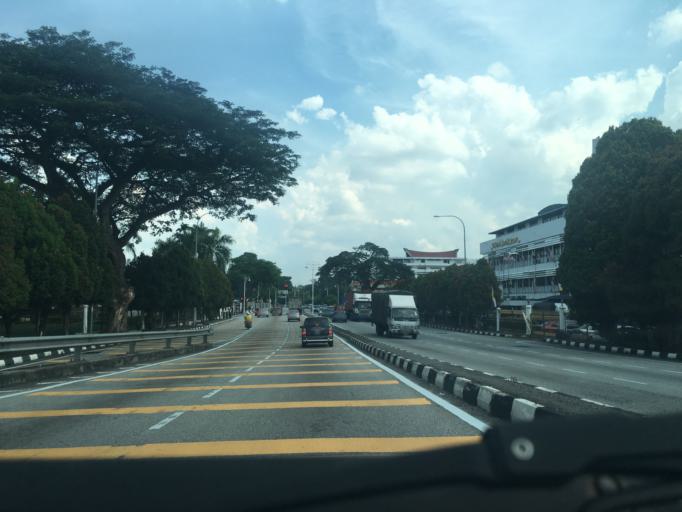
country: MY
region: Perak
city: Ipoh
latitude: 4.6071
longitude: 101.0781
